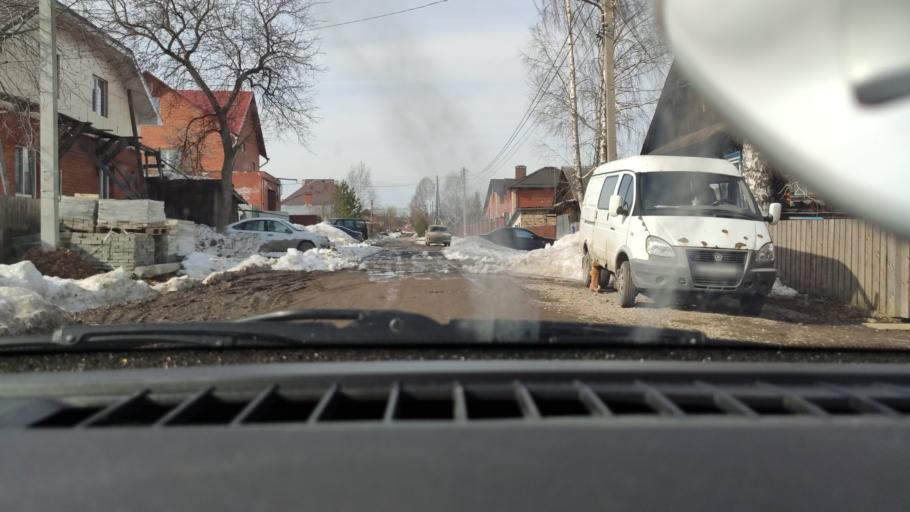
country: RU
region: Perm
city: Perm
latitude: 58.0149
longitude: 56.3194
